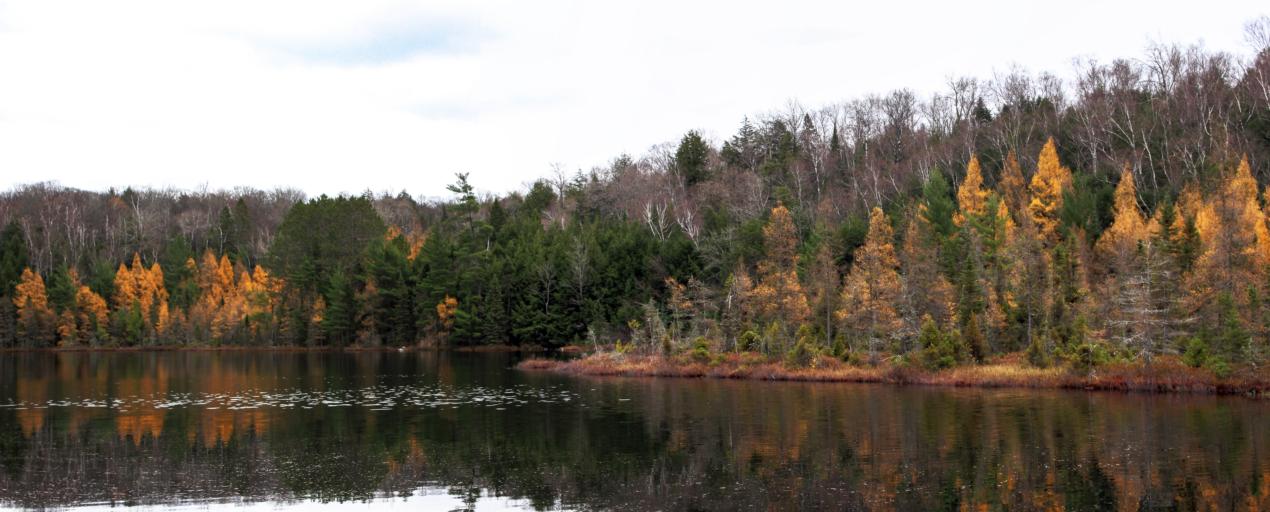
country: US
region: Wisconsin
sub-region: Vilas County
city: Eagle River
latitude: 45.9135
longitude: -89.0387
